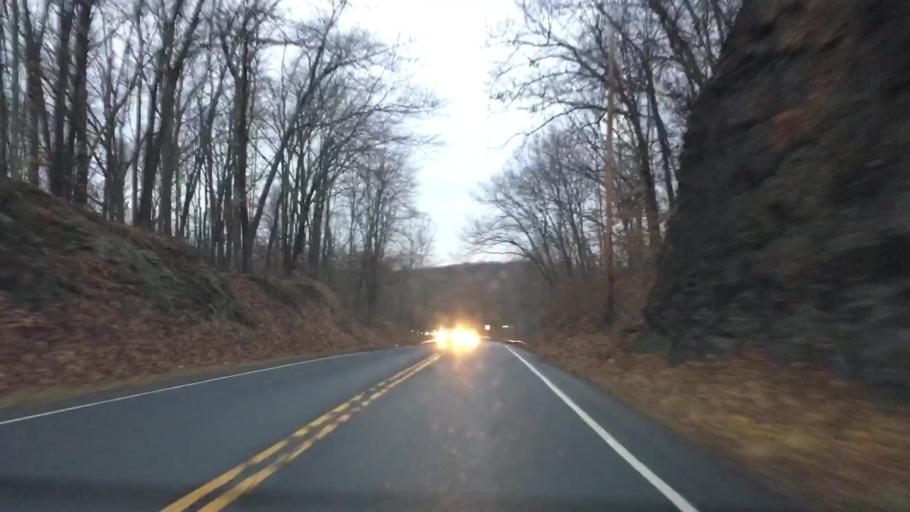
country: US
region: New York
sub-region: Dutchess County
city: Hillside Lake
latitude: 41.6443
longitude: -73.8077
